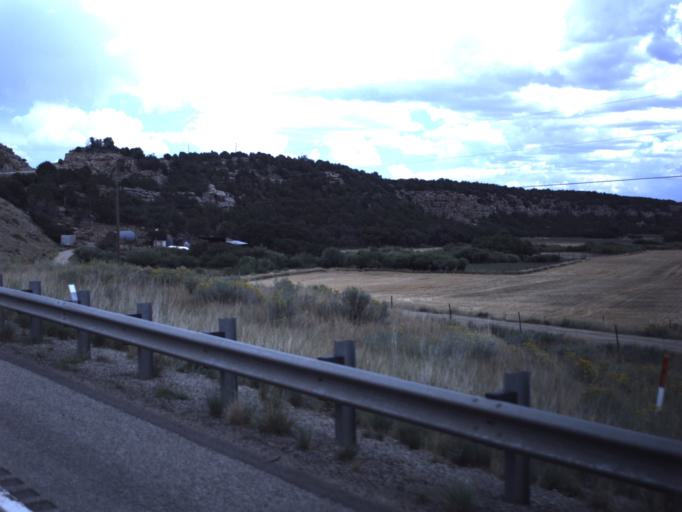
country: US
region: Utah
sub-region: San Juan County
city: Monticello
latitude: 37.7867
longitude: -109.3481
